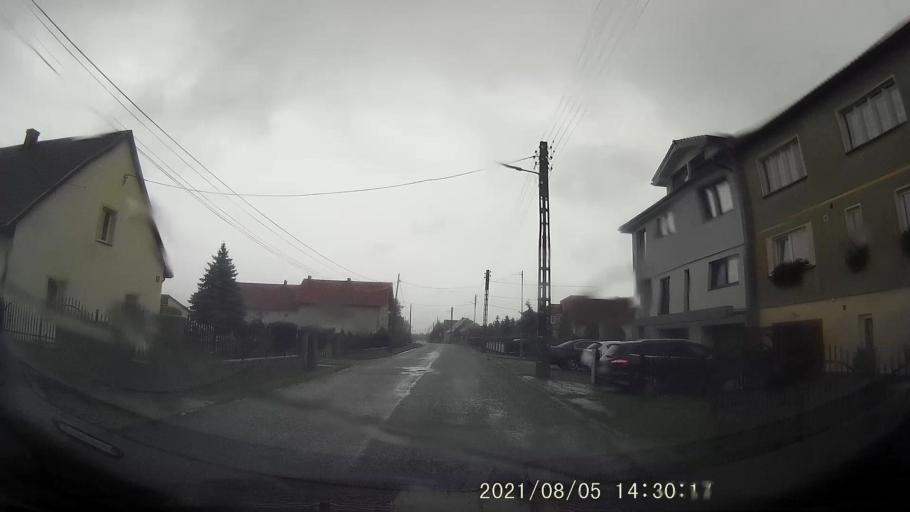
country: PL
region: Opole Voivodeship
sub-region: Powiat nyski
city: Korfantow
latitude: 50.4845
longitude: 17.5553
